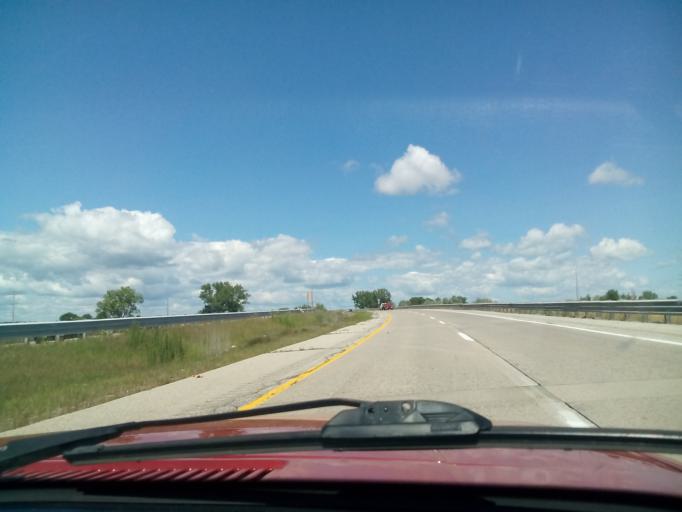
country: US
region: Michigan
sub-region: Bay County
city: Bay City
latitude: 43.6166
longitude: -83.9475
